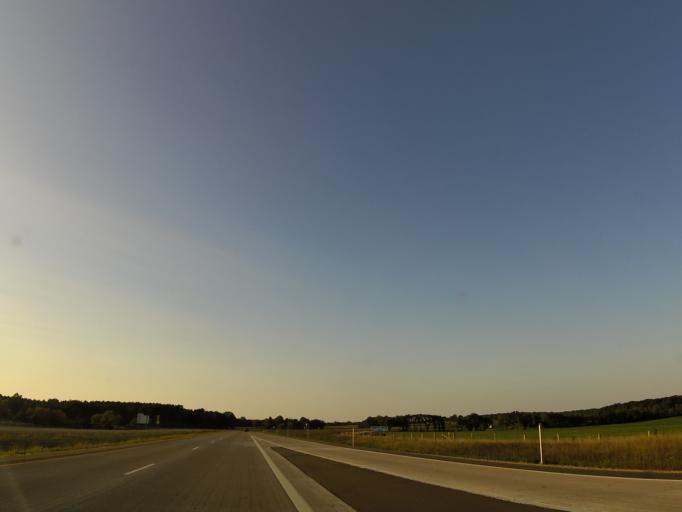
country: US
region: Minnesota
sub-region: Washington County
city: Stillwater
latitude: 45.0629
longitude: -92.7811
